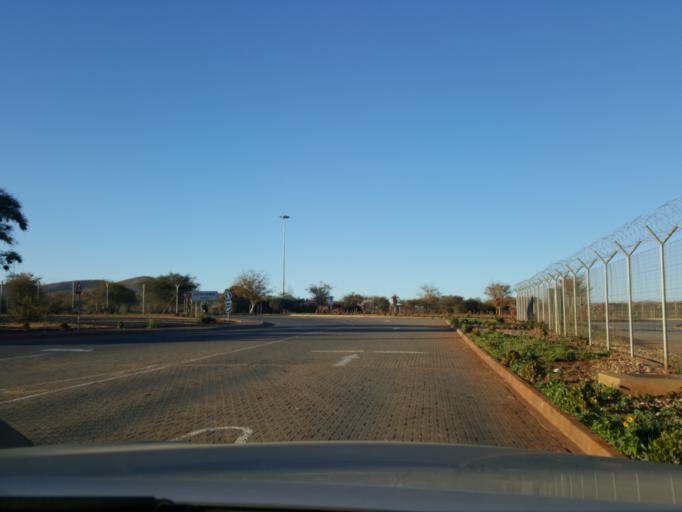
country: BW
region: South East
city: Lobatse
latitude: -25.2765
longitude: 25.7139
